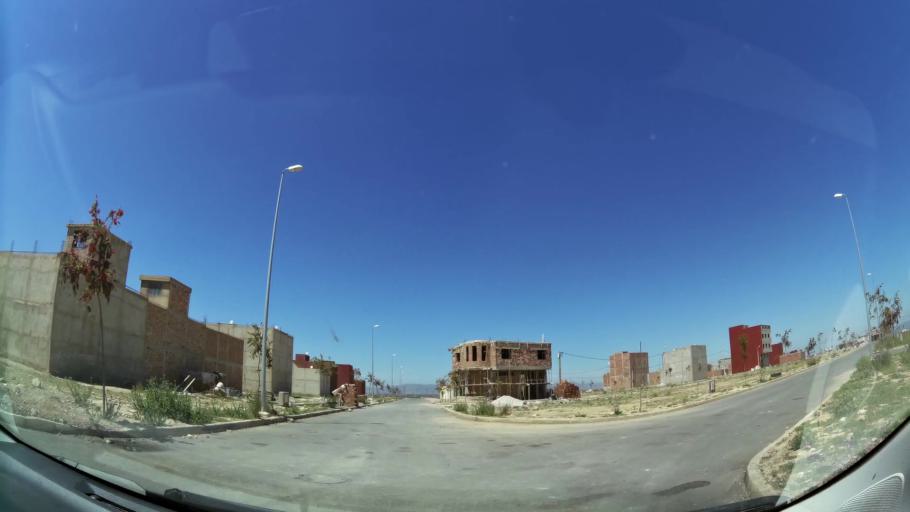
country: MA
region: Oriental
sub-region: Oujda-Angad
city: Oujda
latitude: 34.6844
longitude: -1.8647
